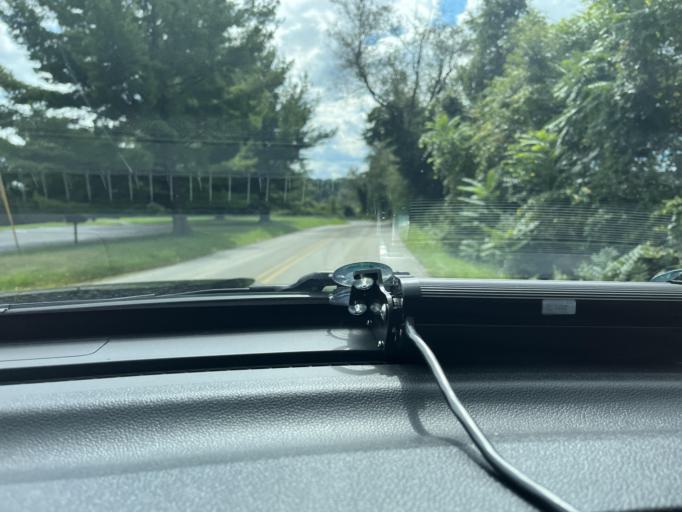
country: US
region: Pennsylvania
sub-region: Fayette County
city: South Uniontown
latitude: 39.9045
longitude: -79.7690
